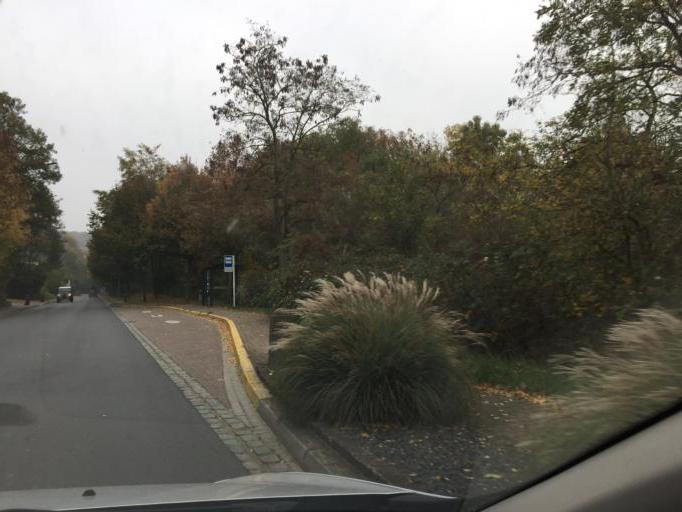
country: LU
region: Luxembourg
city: Moutfort
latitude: 49.5947
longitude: 6.2503
